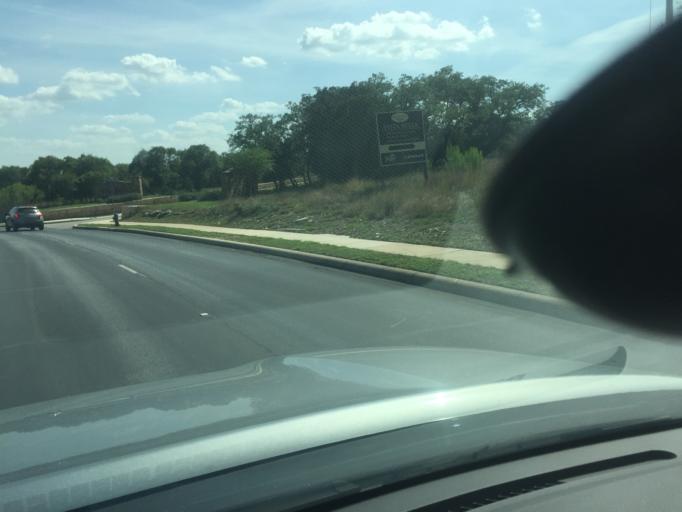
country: US
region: Texas
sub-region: Bexar County
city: Timberwood Park
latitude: 29.6798
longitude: -98.4765
